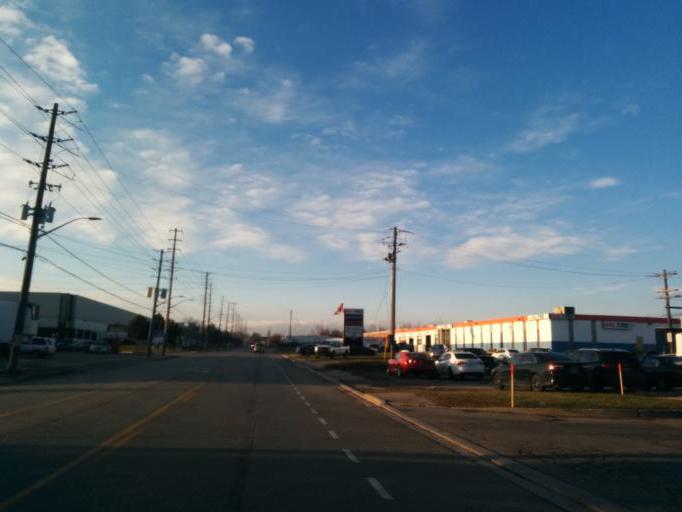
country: CA
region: Ontario
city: Etobicoke
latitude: 43.5987
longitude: -79.5835
